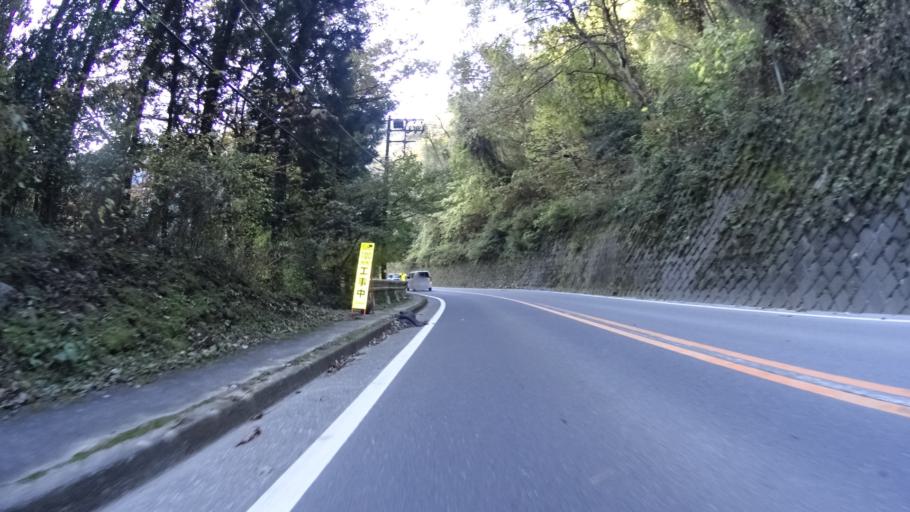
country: JP
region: Tokyo
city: Itsukaichi
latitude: 35.7243
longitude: 139.1452
